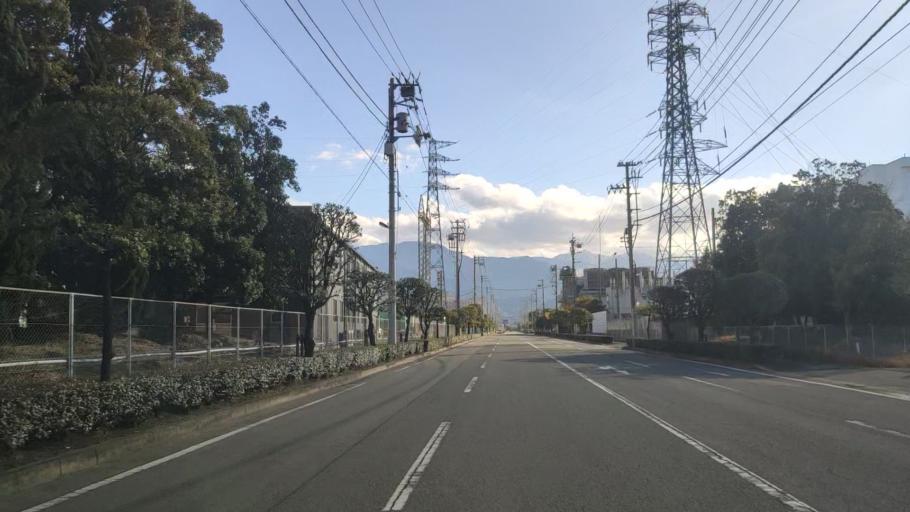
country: JP
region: Ehime
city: Saijo
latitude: 33.9397
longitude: 133.1915
